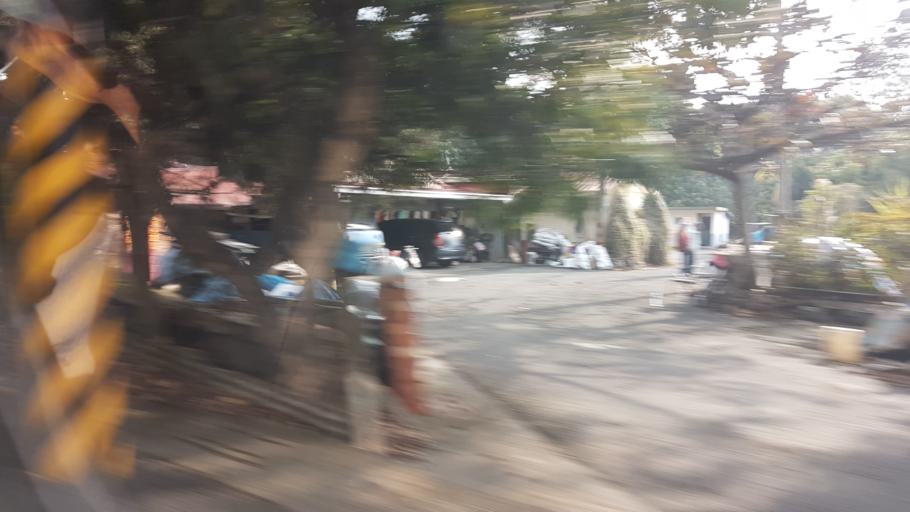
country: TW
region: Taiwan
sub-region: Chiayi
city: Jiayi Shi
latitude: 23.3852
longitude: 120.4377
